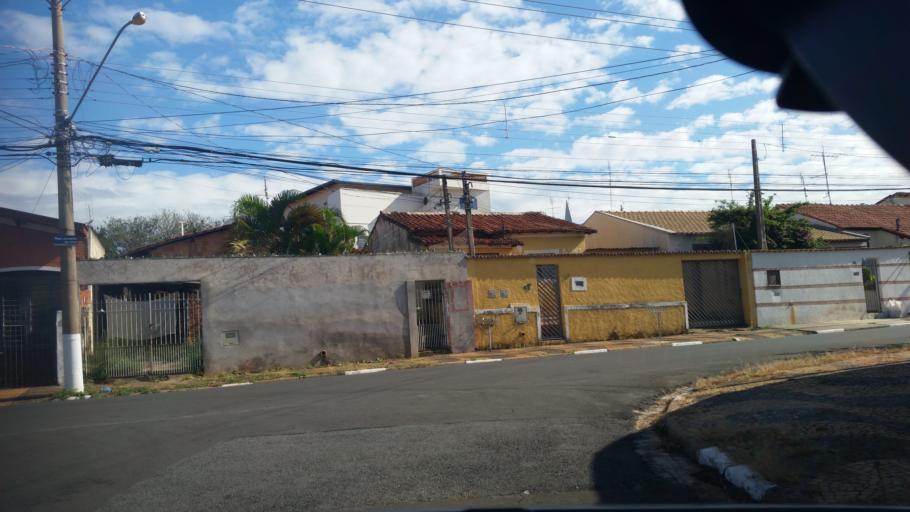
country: BR
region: Sao Paulo
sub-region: Campinas
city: Campinas
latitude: -22.8760
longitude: -47.0427
